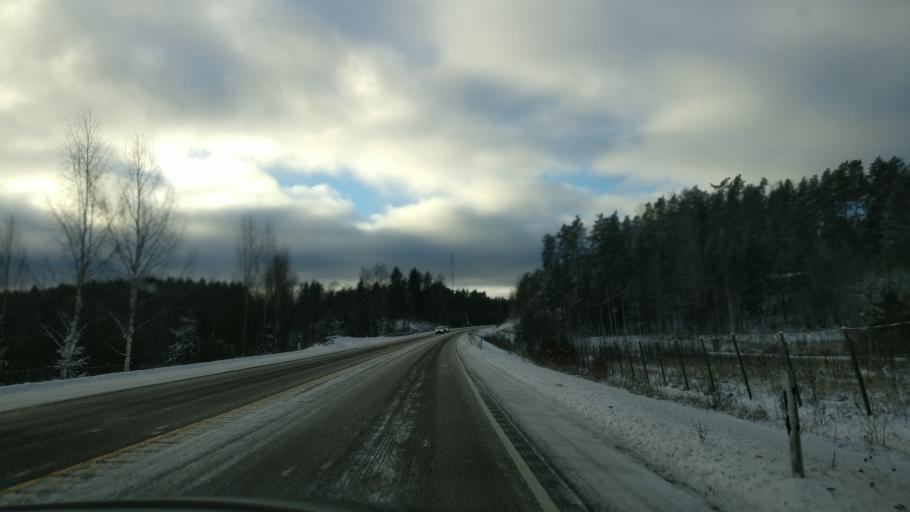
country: FI
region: Southern Savonia
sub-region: Mikkeli
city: Pertunmaa
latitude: 61.3692
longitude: 26.2828
